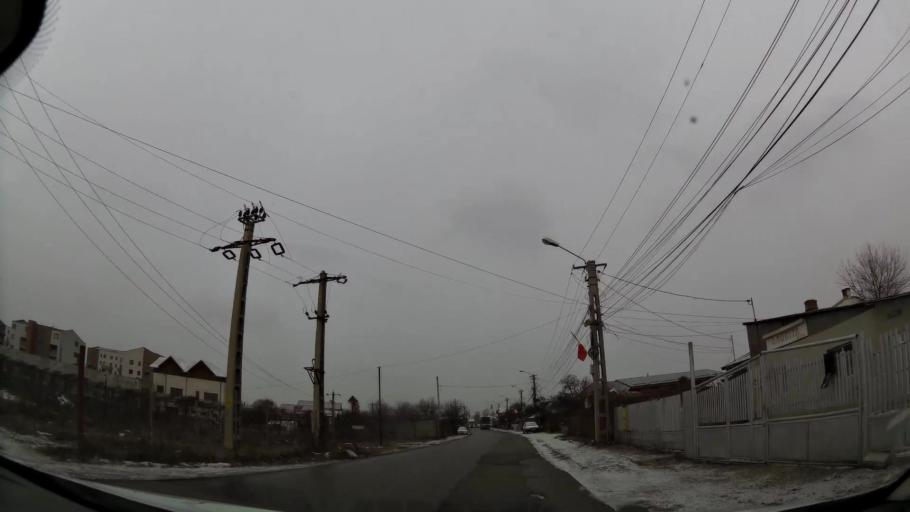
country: RO
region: Dambovita
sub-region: Municipiul Targoviste
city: Targoviste
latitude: 44.9404
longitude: 25.4634
